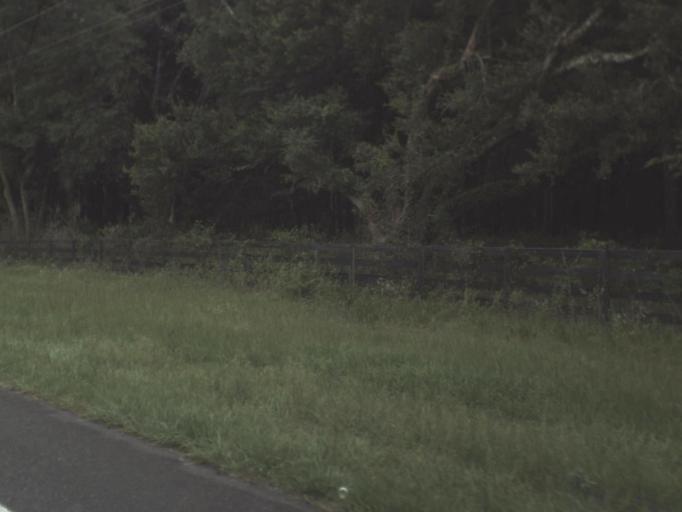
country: US
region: Florida
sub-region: Levy County
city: Williston
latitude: 29.2896
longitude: -82.4464
